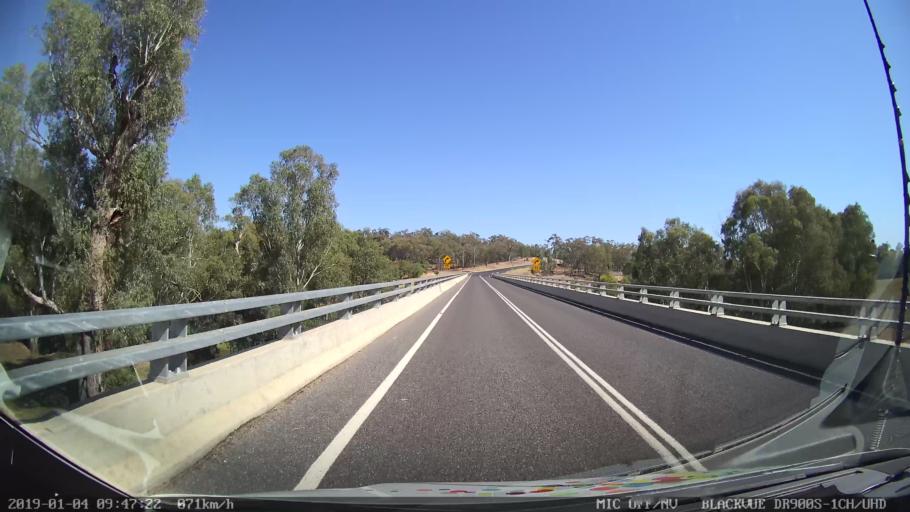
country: AU
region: New South Wales
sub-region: Cabonne
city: Canowindra
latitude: -33.6070
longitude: 148.4322
